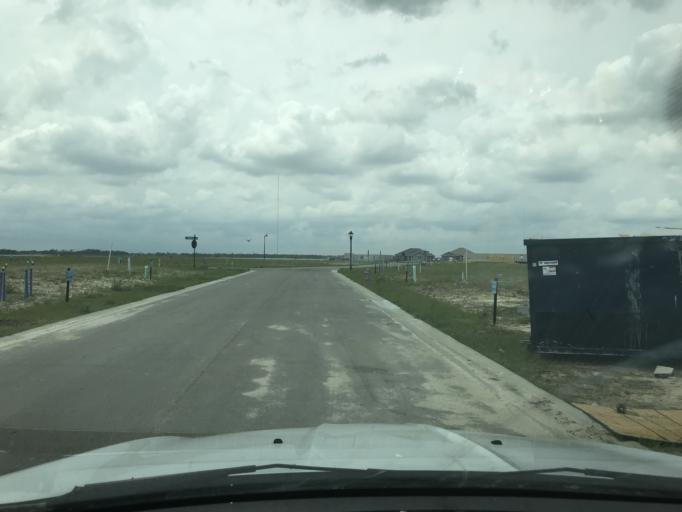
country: US
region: Florida
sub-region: Lee County
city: Olga
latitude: 26.7870
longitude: -81.7363
